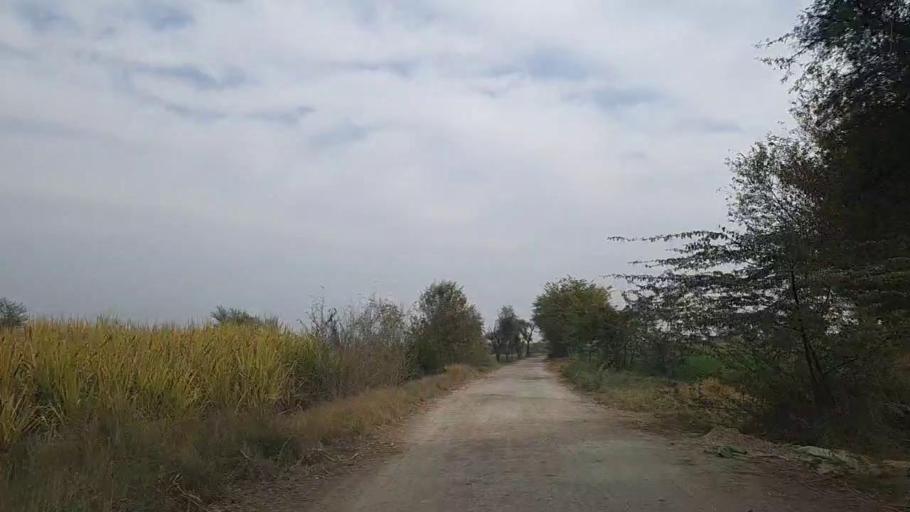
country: PK
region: Sindh
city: Daur
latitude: 26.4243
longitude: 68.4577
